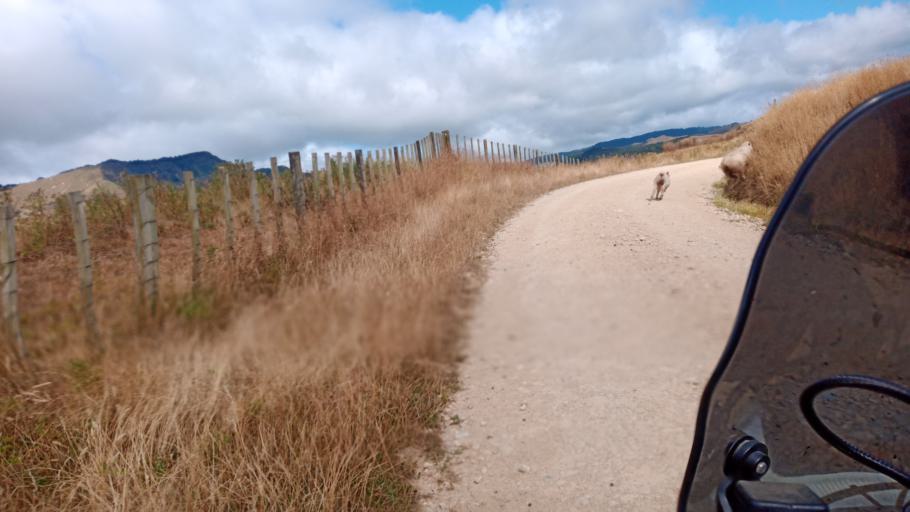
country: NZ
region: Hawke's Bay
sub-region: Wairoa District
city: Wairoa
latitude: -38.6115
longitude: 177.4337
